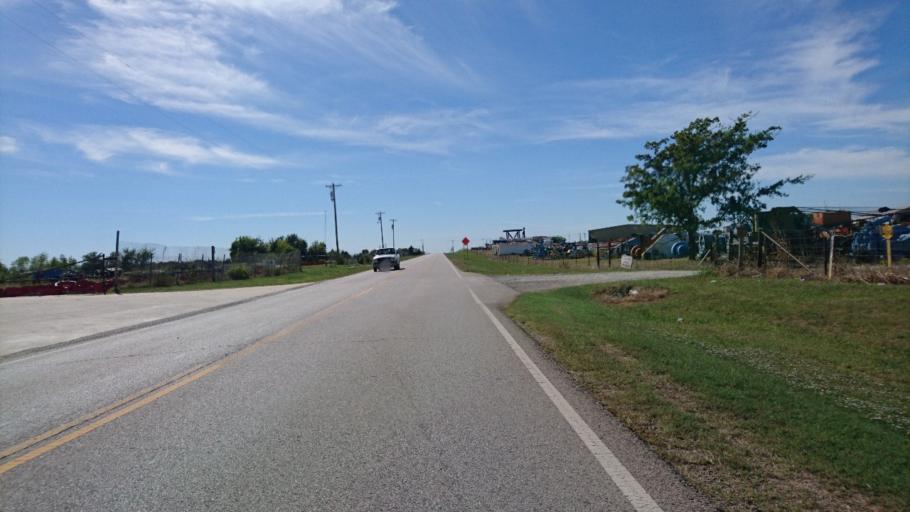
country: US
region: Oklahoma
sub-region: Lincoln County
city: Stroud
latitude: 35.7460
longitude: -96.6941
